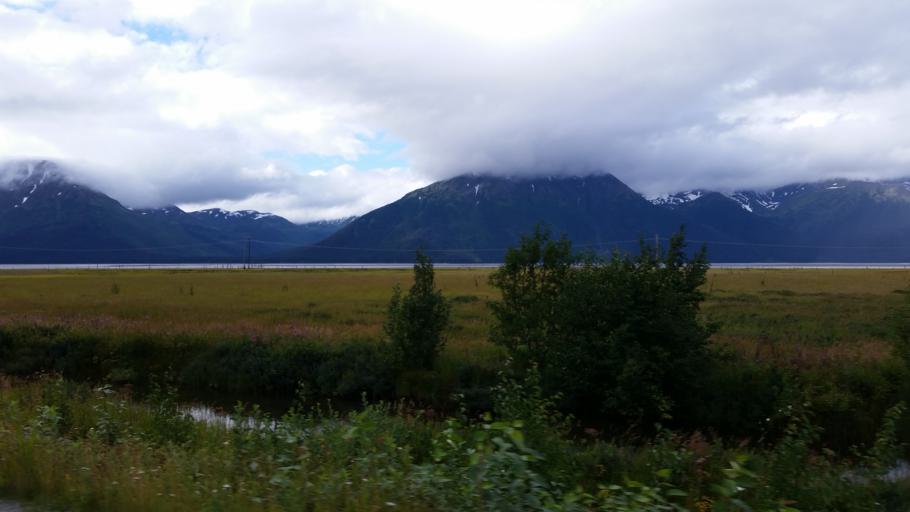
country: US
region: Alaska
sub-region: Anchorage Municipality
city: Girdwood
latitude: 60.9368
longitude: -149.1613
